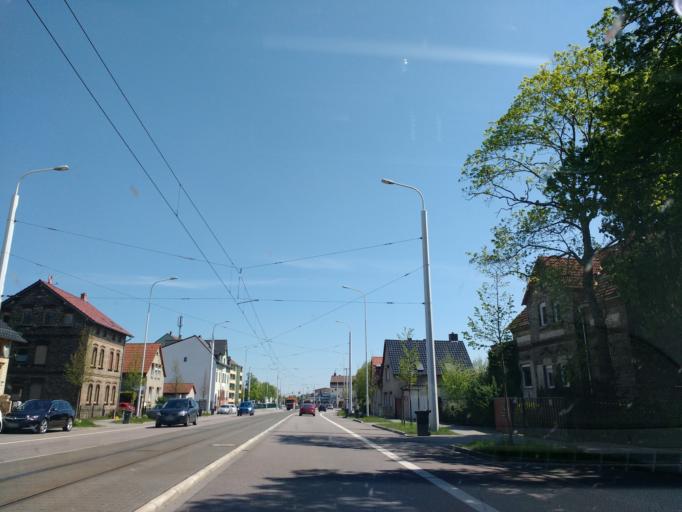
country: DE
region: Saxony-Anhalt
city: Dolbau
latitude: 51.4788
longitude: 12.0288
